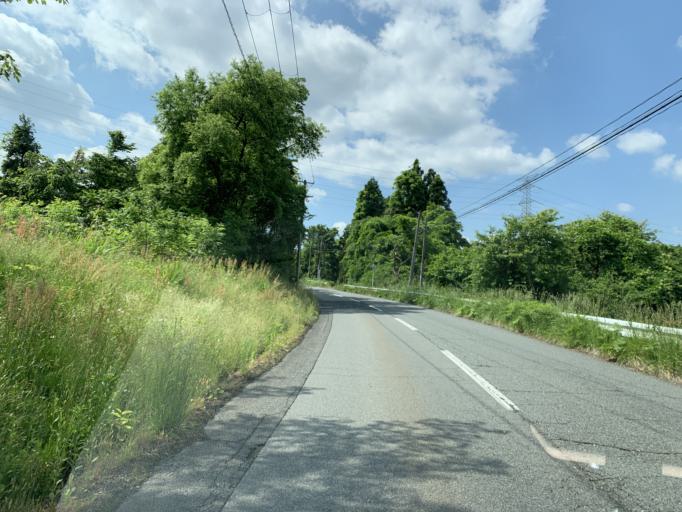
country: JP
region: Miyagi
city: Furukawa
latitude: 38.7801
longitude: 140.9587
